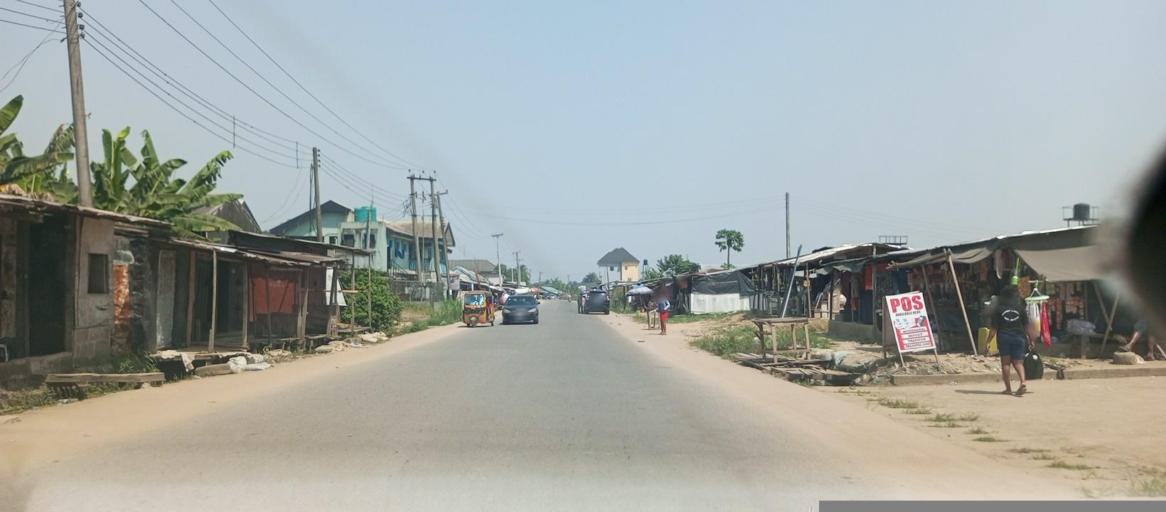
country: NG
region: Rivers
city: Emuoha
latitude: 4.9133
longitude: 6.9134
